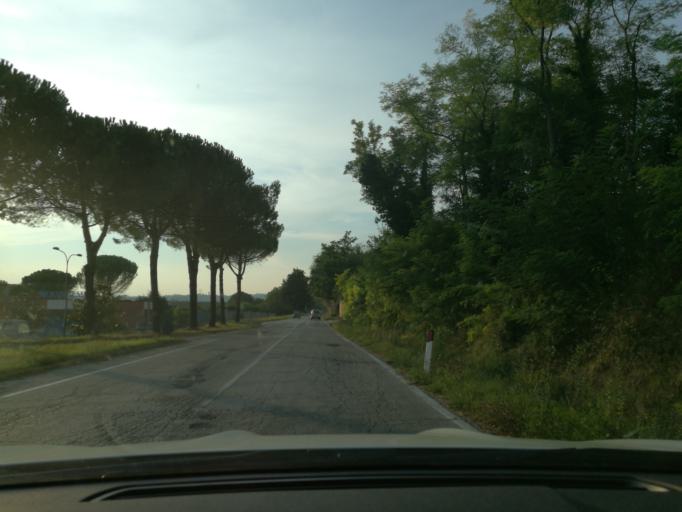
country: IT
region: Umbria
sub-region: Provincia di Terni
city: San Gemini
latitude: 42.6331
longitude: 12.5518
